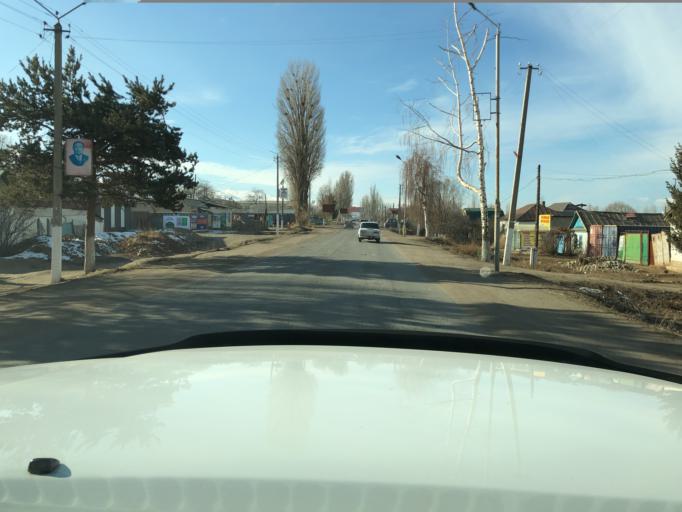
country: KG
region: Ysyk-Koel
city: Pokrovka
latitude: 42.3377
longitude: 77.9950
